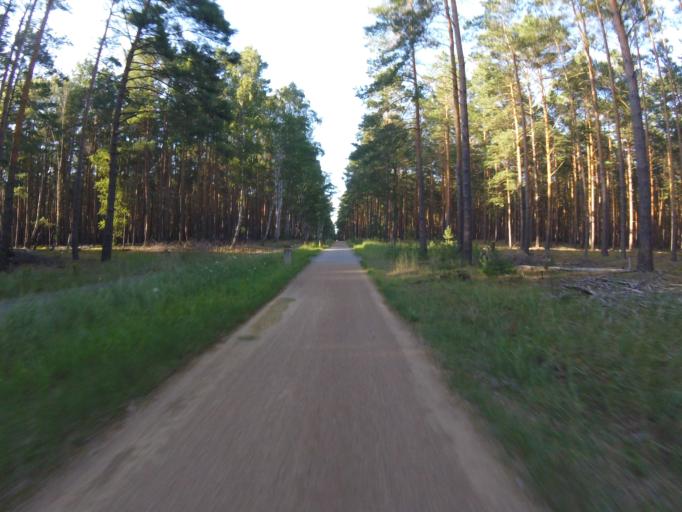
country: DE
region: Brandenburg
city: Munchehofe
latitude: 52.2035
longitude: 13.7676
